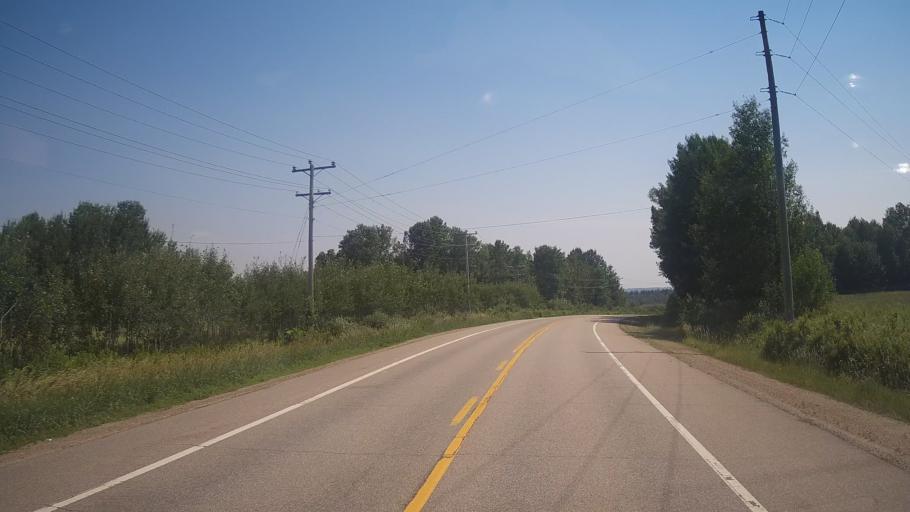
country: CA
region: Ontario
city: Pembroke
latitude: 45.8305
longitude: -77.0134
